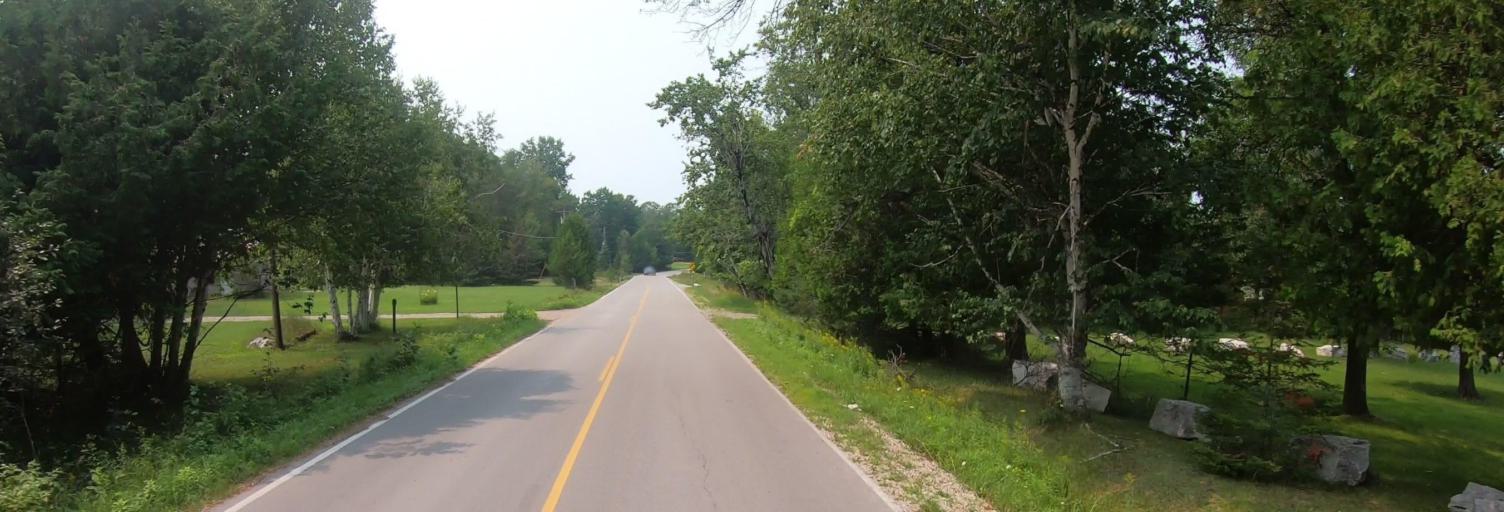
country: CA
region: Ontario
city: Thessalon
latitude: 46.0359
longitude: -83.7029
